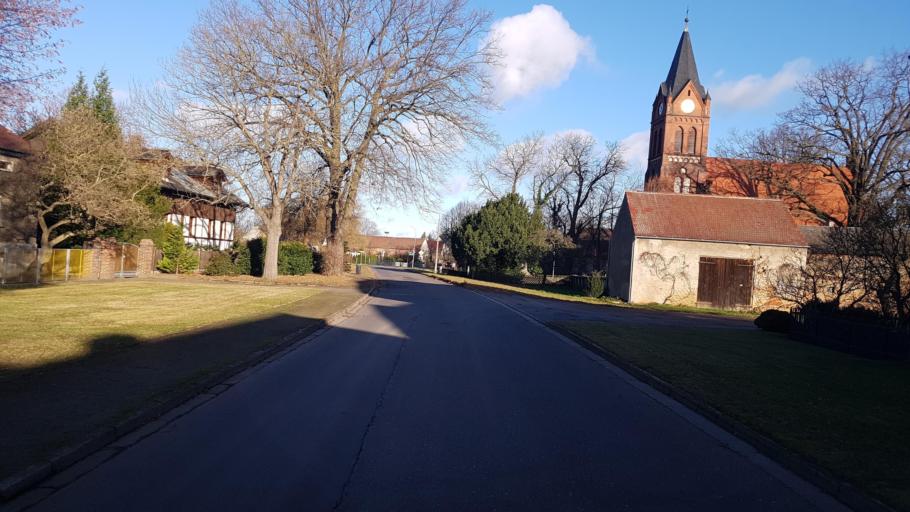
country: DE
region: Brandenburg
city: Forst
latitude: 51.7791
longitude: 14.6463
